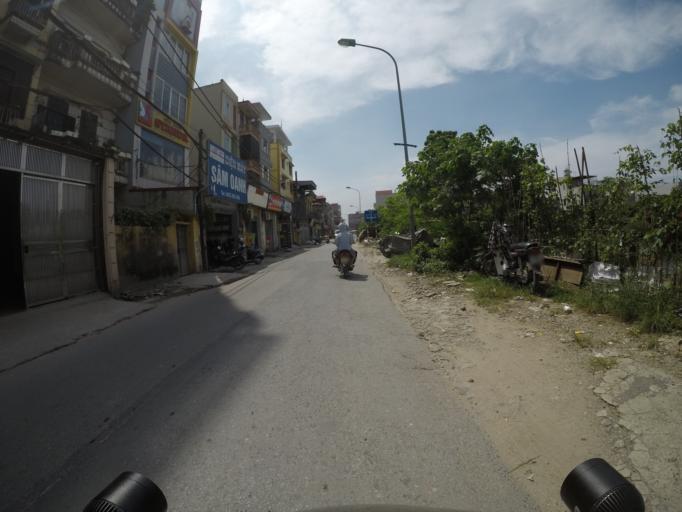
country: VN
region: Ha Noi
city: Troi
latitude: 21.0718
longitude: 105.7085
